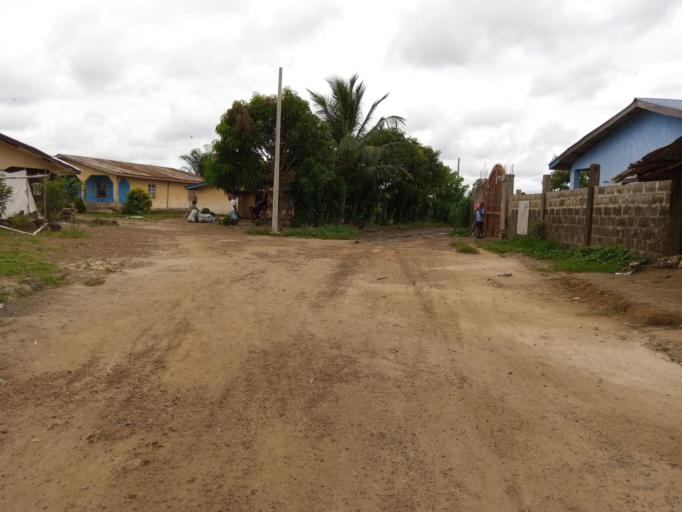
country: SL
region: Southern Province
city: Moyamba
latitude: 8.1685
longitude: -12.4216
